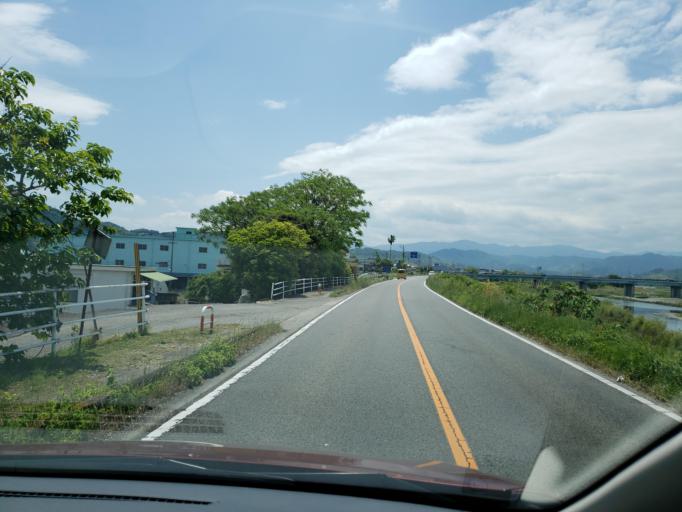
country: JP
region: Tokushima
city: Tokushima-shi
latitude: 34.0757
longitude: 134.5014
